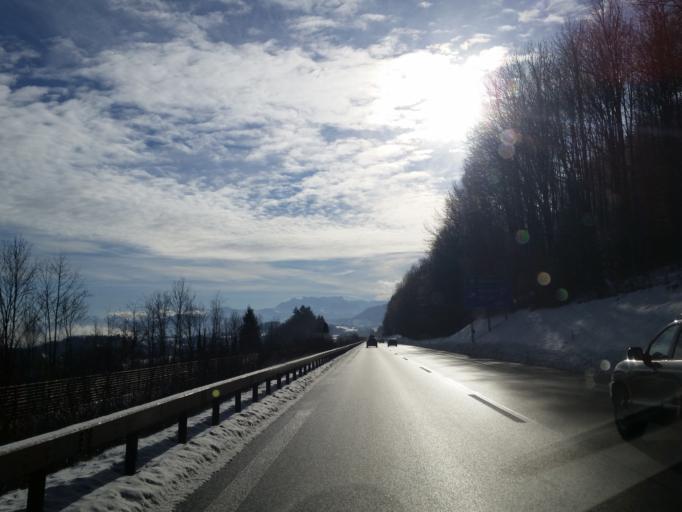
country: CH
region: Zurich
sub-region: Bezirk Horgen
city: Horgen / Allmend
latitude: 47.2464
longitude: 8.6001
